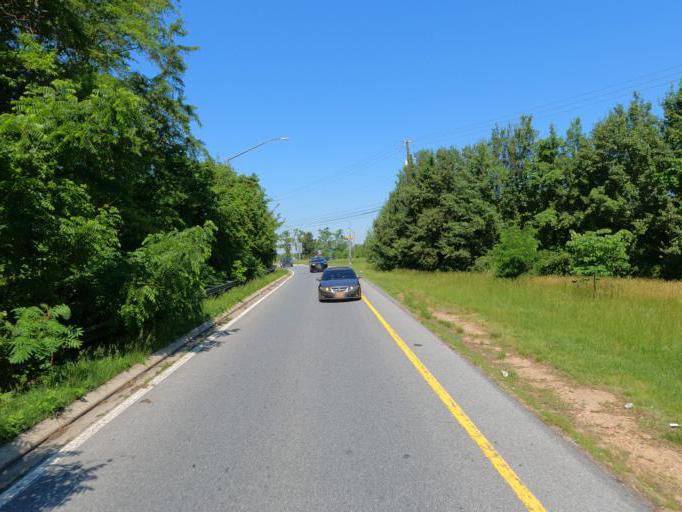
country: US
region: Maryland
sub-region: Montgomery County
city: Germantown
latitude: 39.1829
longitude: -77.2565
